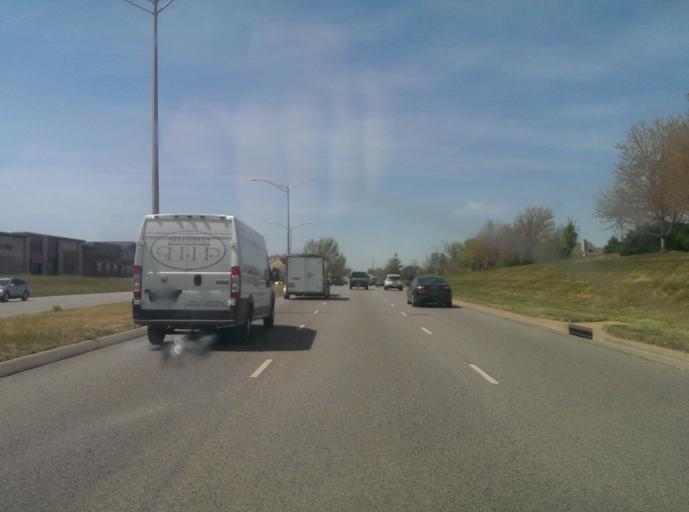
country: US
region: Kansas
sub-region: Johnson County
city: Leawood
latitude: 38.8838
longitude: -94.6496
